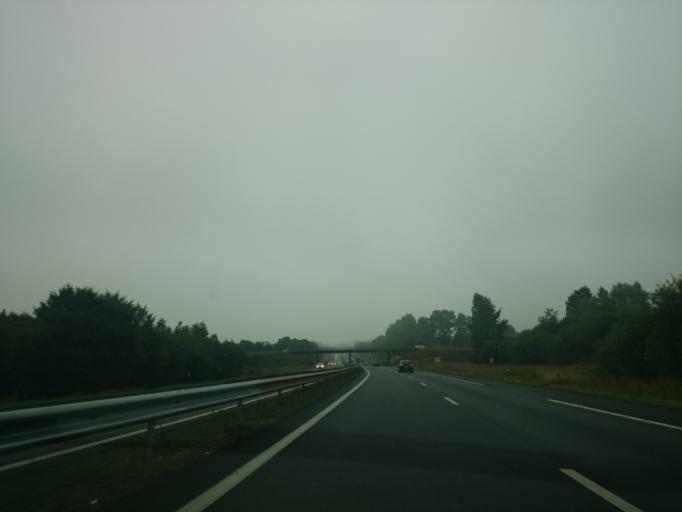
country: FR
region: Brittany
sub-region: Departement d'Ille-et-Vilaine
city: Laille
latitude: 47.9927
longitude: -1.6954
